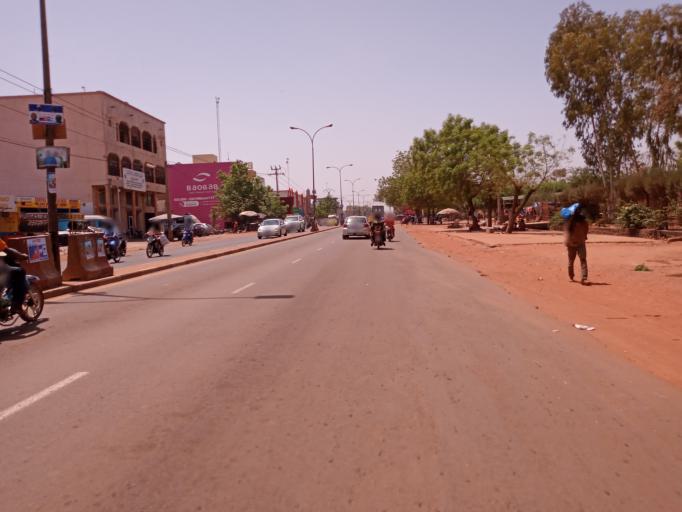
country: ML
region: Bamako
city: Bamako
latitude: 12.6646
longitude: -7.9397
